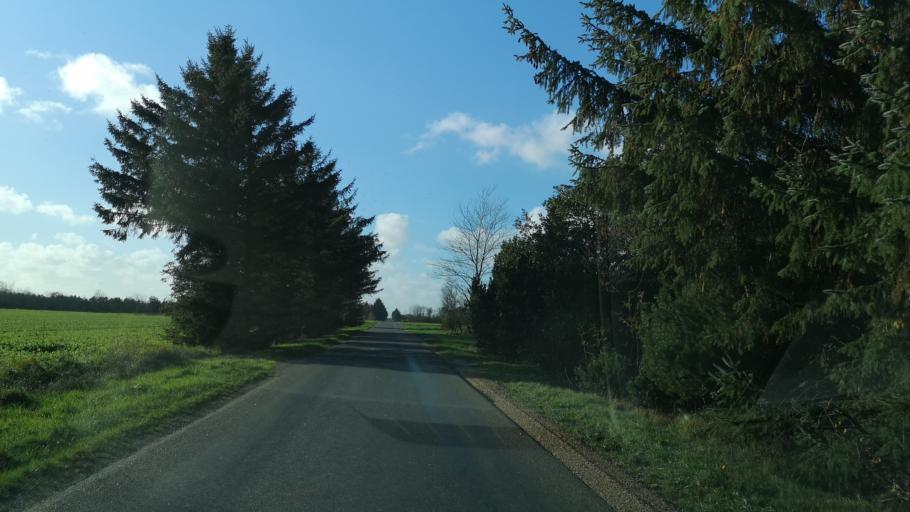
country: DK
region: Central Jutland
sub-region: Ringkobing-Skjern Kommune
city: Skjern
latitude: 55.8363
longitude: 8.3620
